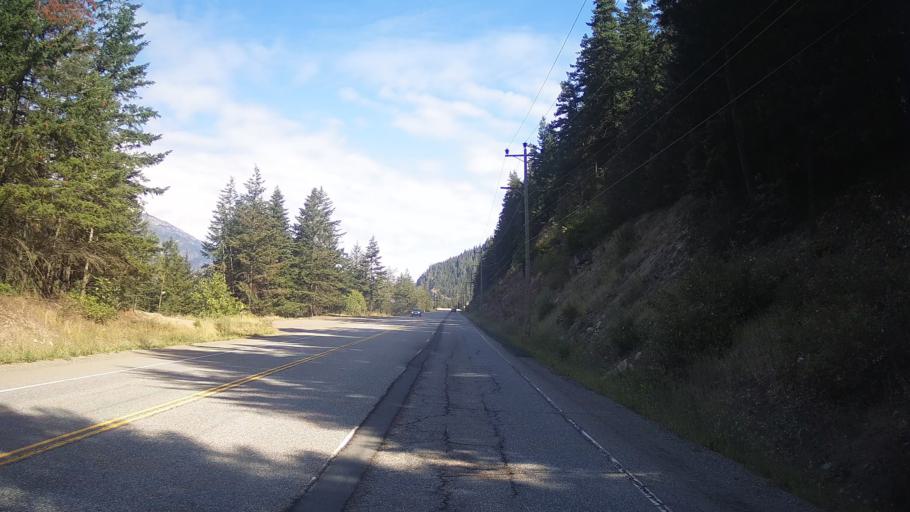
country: CA
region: British Columbia
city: Hope
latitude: 50.0578
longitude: -121.5431
